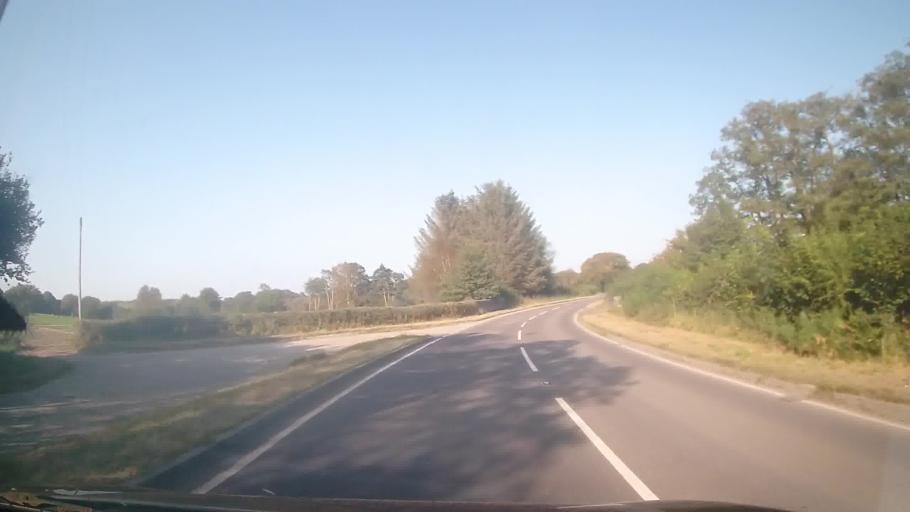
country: GB
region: Wales
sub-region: County of Ceredigion
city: Llangybi
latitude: 52.1856
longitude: -3.9986
